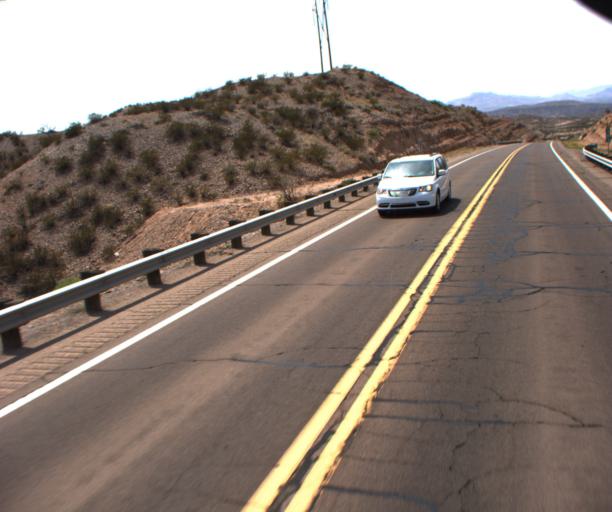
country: US
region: Arizona
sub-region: Greenlee County
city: Clifton
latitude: 32.7555
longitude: -109.1313
